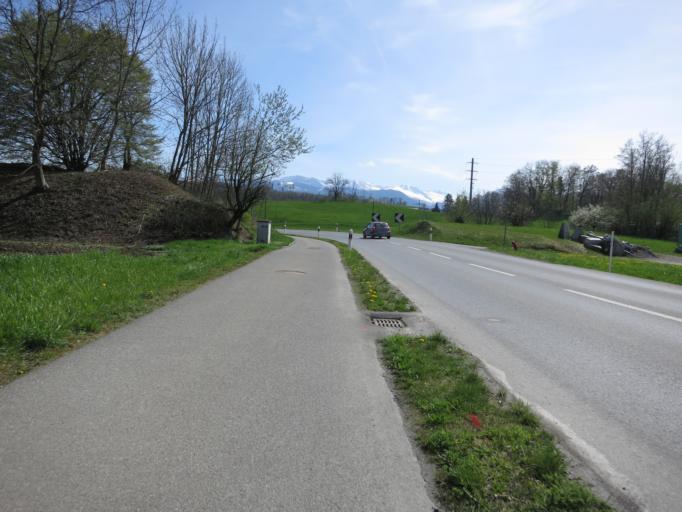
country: CH
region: Zurich
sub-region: Bezirk Hinwil
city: Rueti / Oberdorf
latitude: 47.2498
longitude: 8.8776
